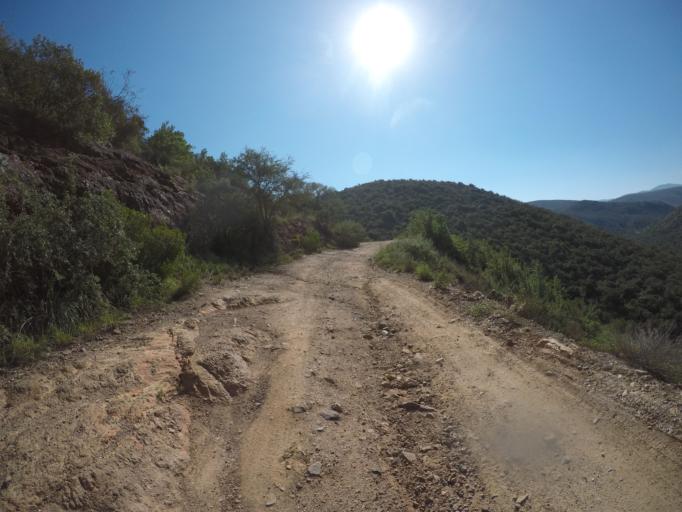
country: ZA
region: Eastern Cape
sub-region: Cacadu District Municipality
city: Kareedouw
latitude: -33.6555
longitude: 24.4252
